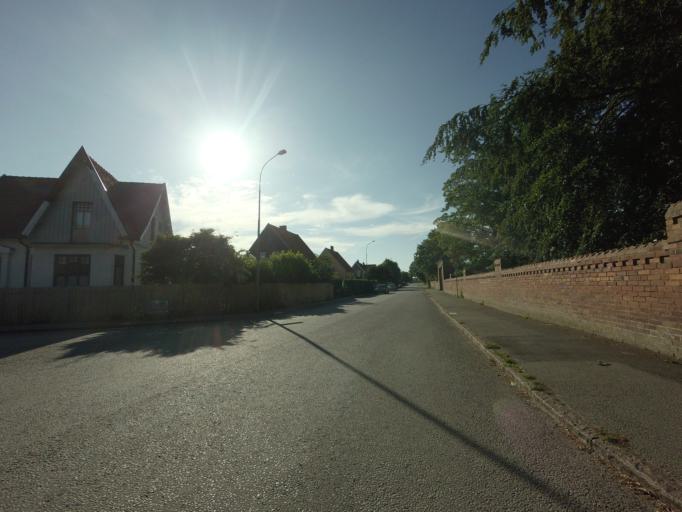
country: SE
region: Skane
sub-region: Hoganas Kommun
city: Hoganas
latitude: 56.1973
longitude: 12.5599
